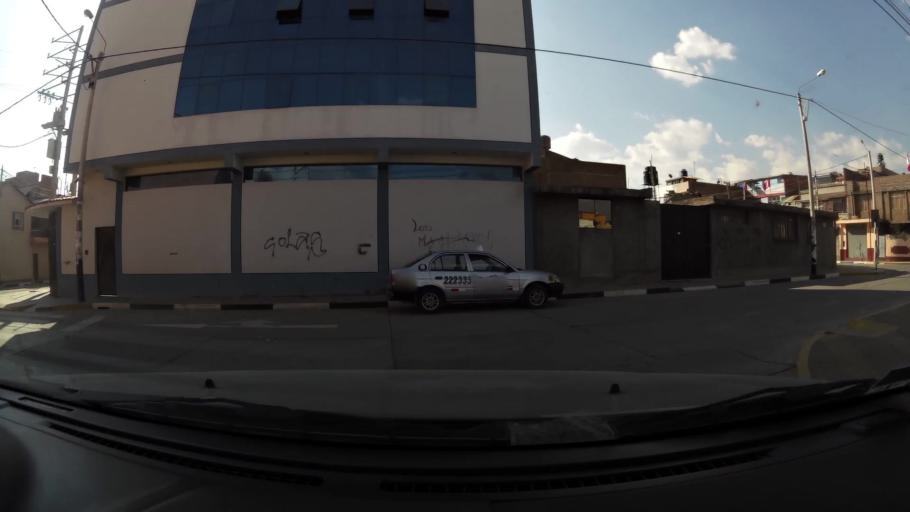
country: PE
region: Junin
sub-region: Provincia de Huancayo
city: El Tambo
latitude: -12.0625
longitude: -75.2243
